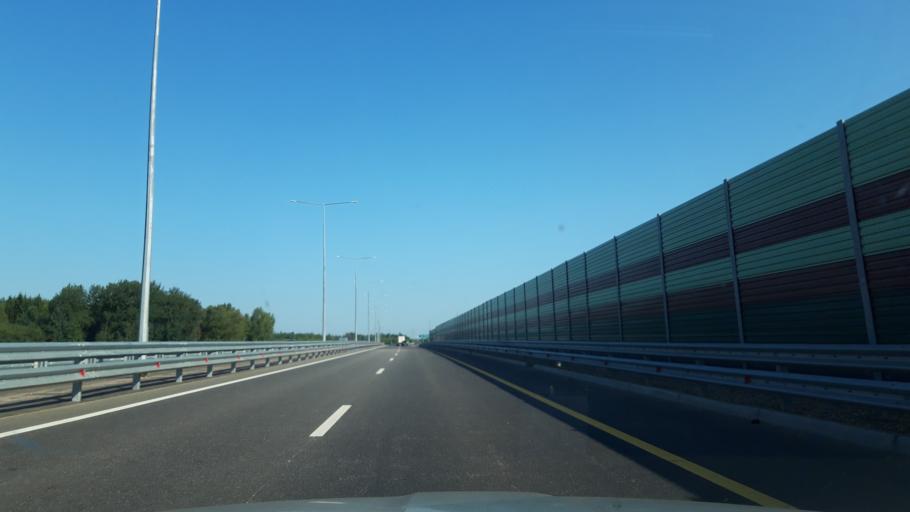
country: RU
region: Moskovskaya
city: Spas-Zaulok
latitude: 56.4913
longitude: 36.5321
